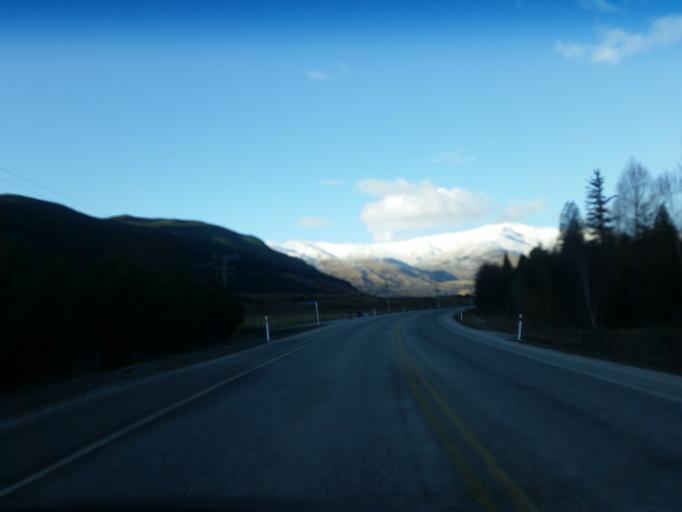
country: NZ
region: Otago
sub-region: Queenstown-Lakes District
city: Arrowtown
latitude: -44.9464
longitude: 168.7693
